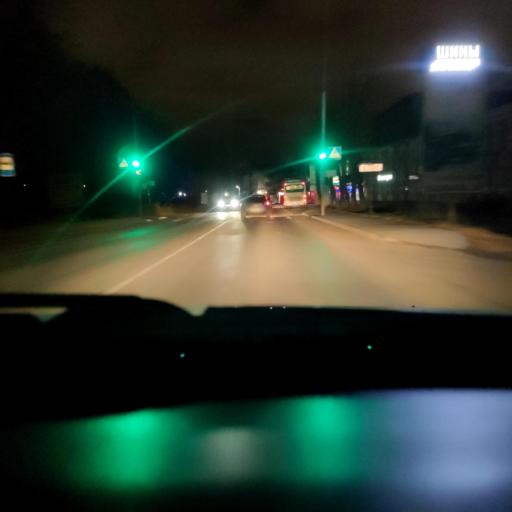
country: RU
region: Perm
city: Perm
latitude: 57.9564
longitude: 56.2166
